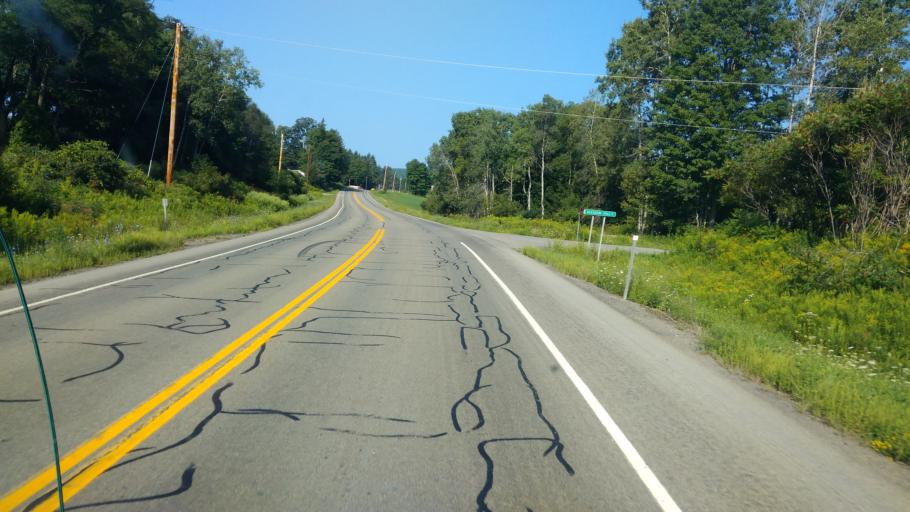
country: US
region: New York
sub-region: Allegany County
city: Friendship
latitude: 42.3049
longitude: -78.1672
